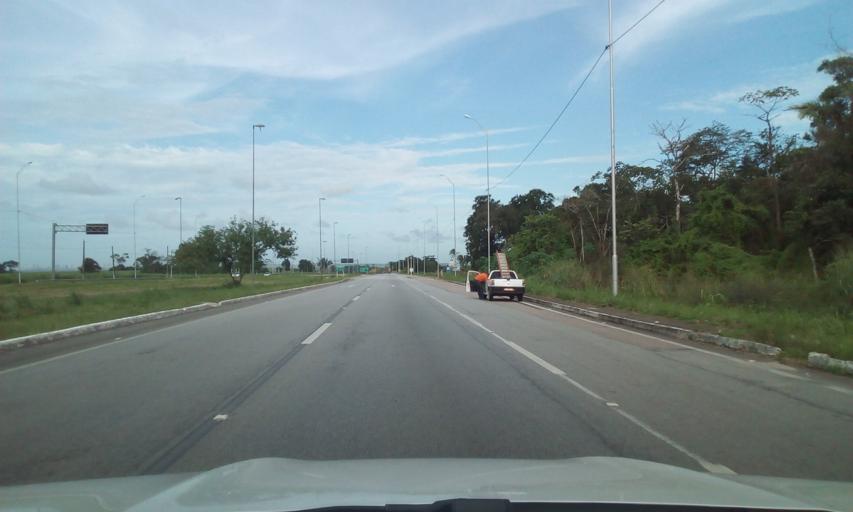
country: BR
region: Paraiba
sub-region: Santa Rita
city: Santa Rita
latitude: -7.0809
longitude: -34.9846
